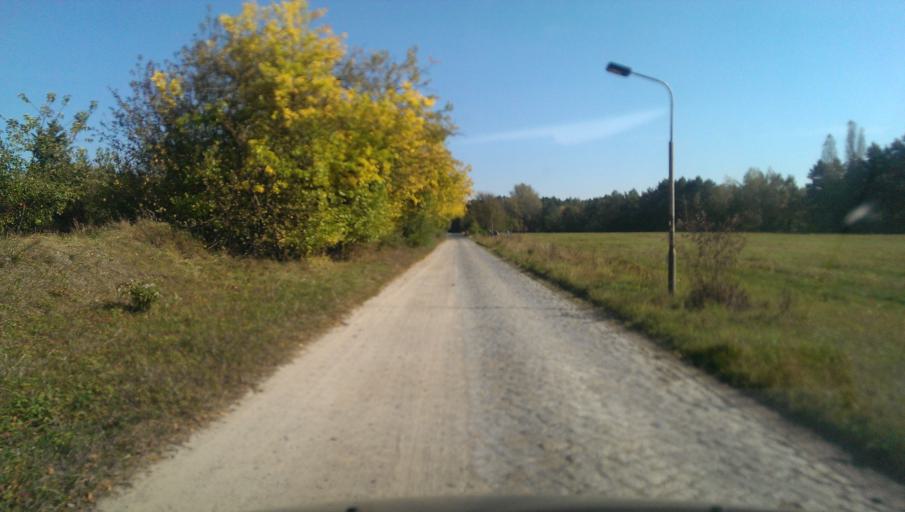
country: DE
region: Brandenburg
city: Am Mellensee
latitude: 52.1915
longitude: 13.3554
